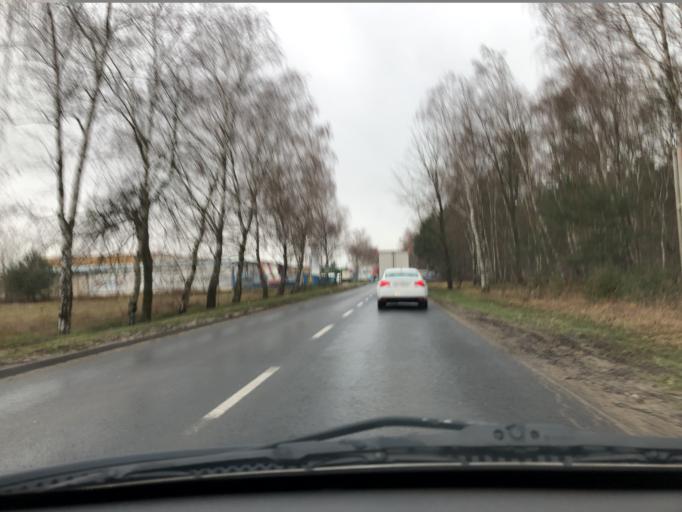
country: PL
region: Greater Poland Voivodeship
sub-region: Powiat poznanski
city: Plewiska
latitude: 52.3925
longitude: 16.8089
